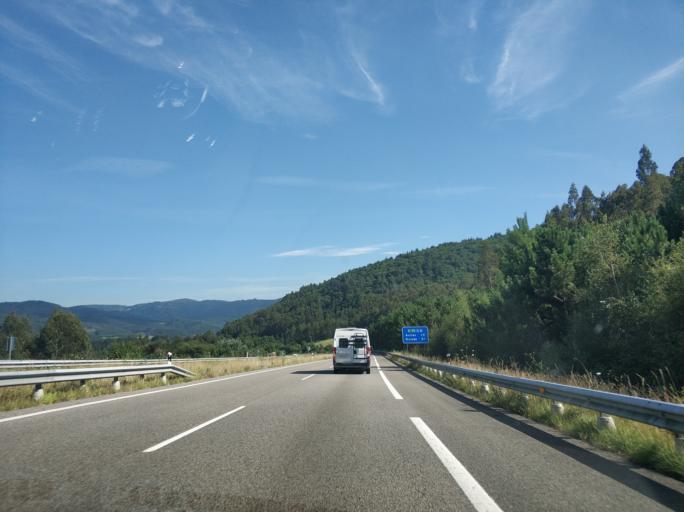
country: ES
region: Asturias
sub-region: Province of Asturias
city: Muros de Nalon
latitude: 43.5316
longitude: -6.1002
